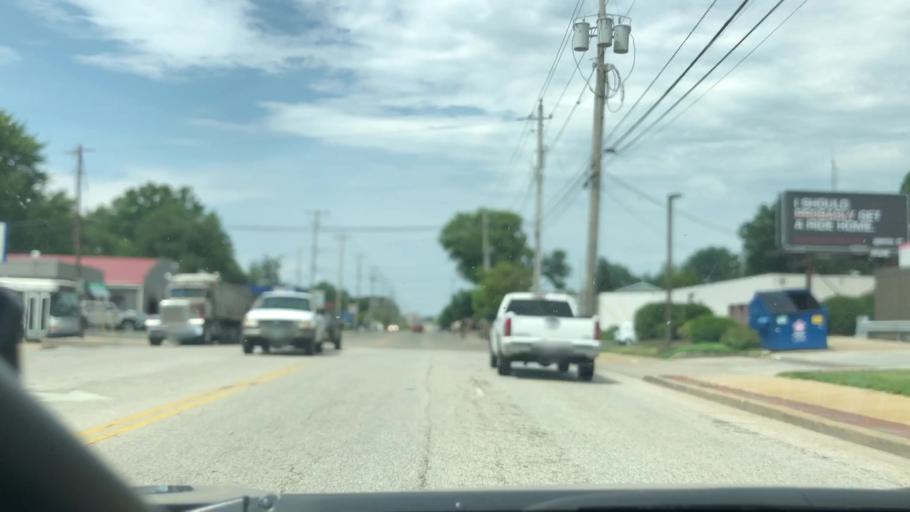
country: US
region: Ohio
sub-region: Summit County
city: Portage Lakes
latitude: 41.0291
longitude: -81.5269
